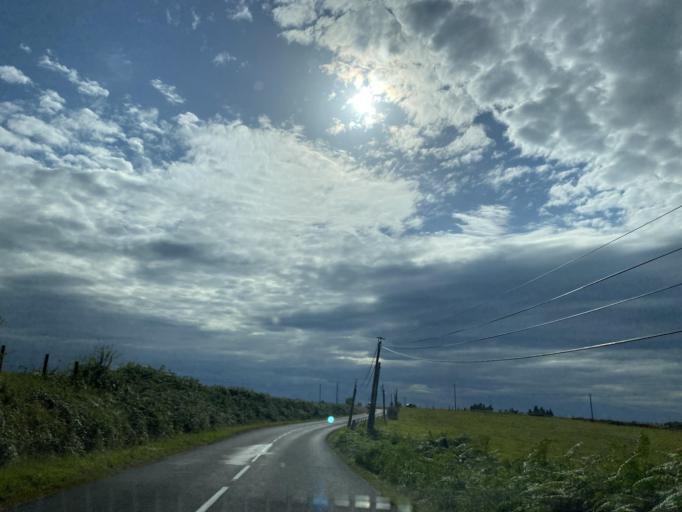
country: FR
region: Auvergne
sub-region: Departement du Puy-de-Dome
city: Courpiere
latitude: 45.7297
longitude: 3.6358
